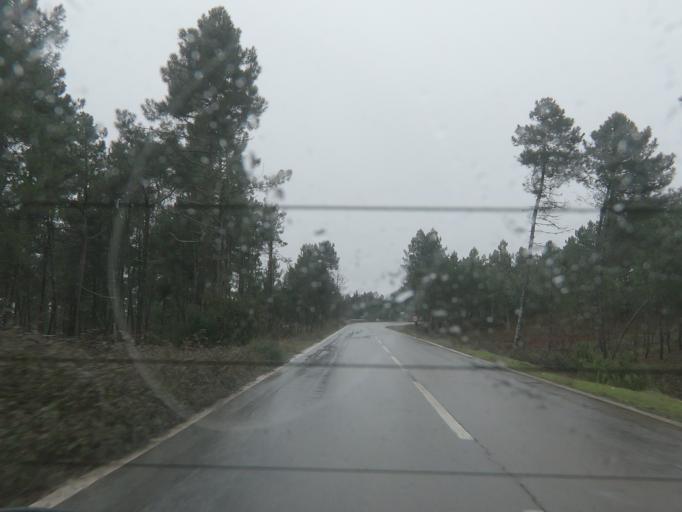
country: PT
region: Vila Real
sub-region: Sabrosa
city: Vilela
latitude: 41.2087
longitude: -7.6802
